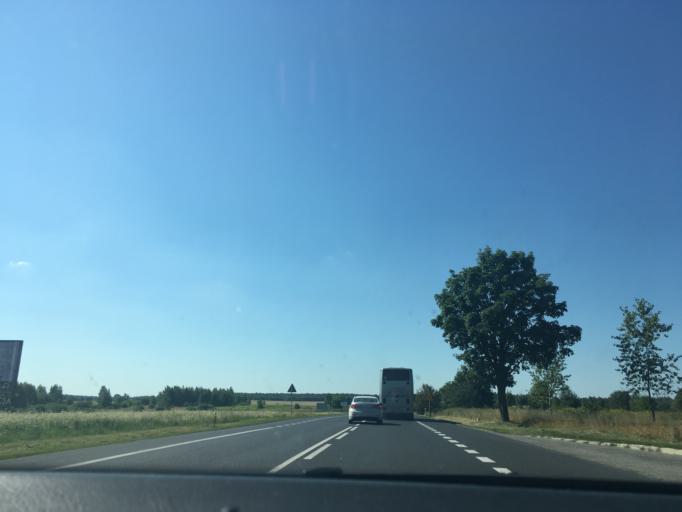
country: PL
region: Lublin Voivodeship
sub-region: Powiat lubartowski
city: Serniki
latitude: 51.4181
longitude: 22.6418
